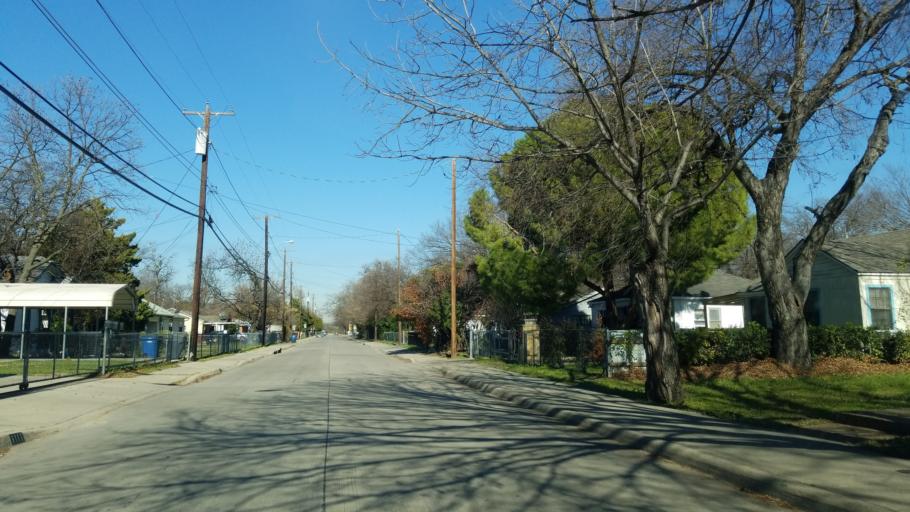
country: US
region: Texas
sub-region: Dallas County
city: Cockrell Hill
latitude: 32.7542
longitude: -96.9114
